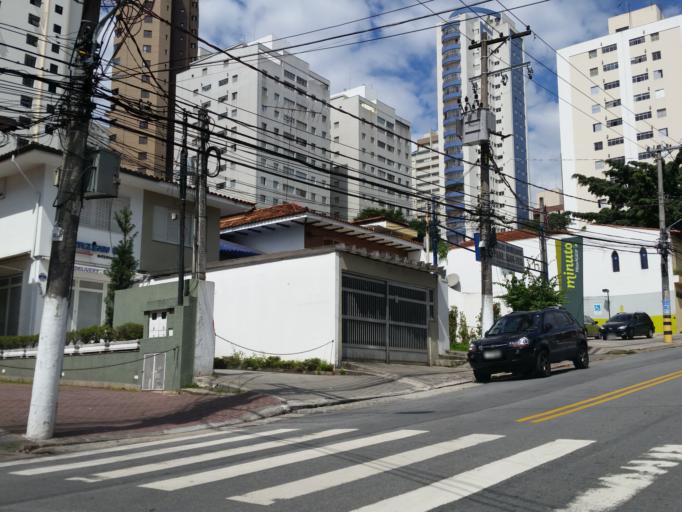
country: BR
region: Sao Paulo
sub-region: Diadema
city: Diadema
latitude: -23.6469
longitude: -46.6702
